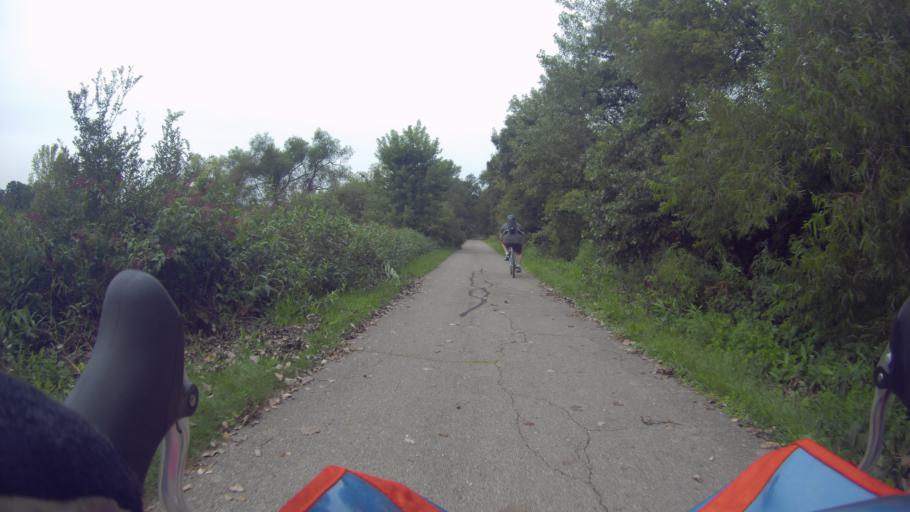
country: US
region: Wisconsin
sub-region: Dane County
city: Verona
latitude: 42.9942
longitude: -89.5048
